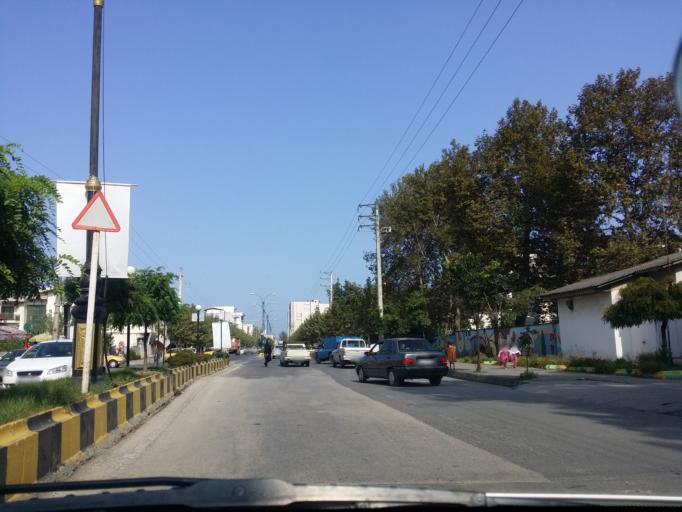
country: IR
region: Mazandaran
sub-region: Nowshahr
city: Nowshahr
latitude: 36.6411
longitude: 51.4905
